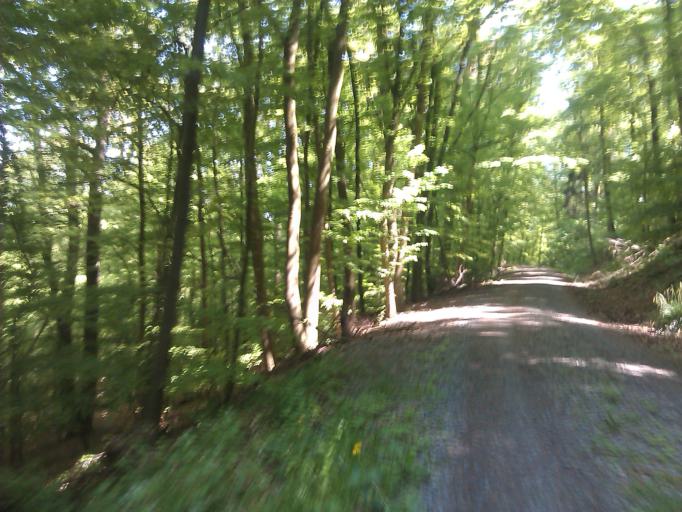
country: DE
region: Baden-Wuerttemberg
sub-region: Karlsruhe Region
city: Sternenfels
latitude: 49.0517
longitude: 8.8743
